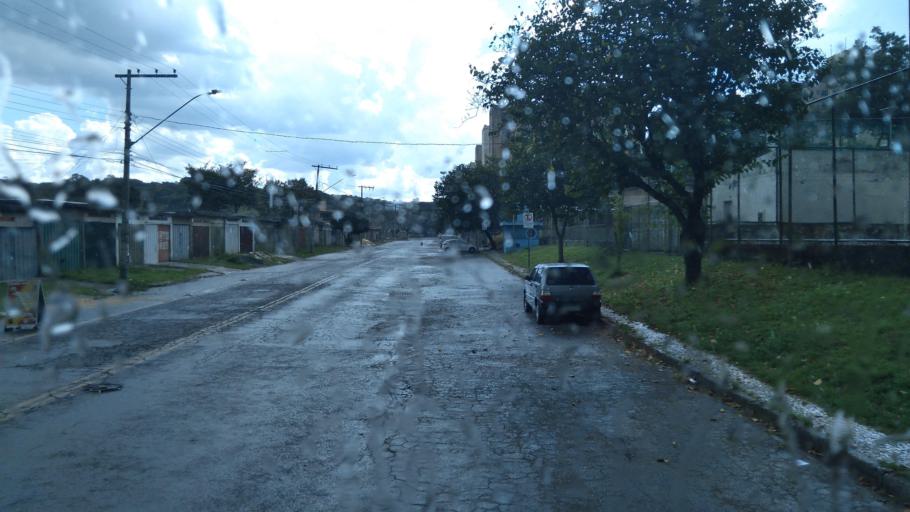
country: BR
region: Minas Gerais
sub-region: Contagem
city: Contagem
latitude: -19.9199
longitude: -44.0103
